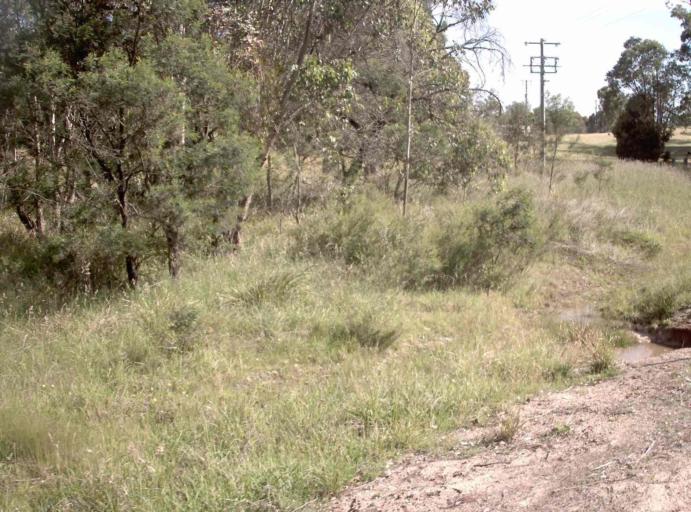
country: AU
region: Victoria
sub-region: East Gippsland
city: Lakes Entrance
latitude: -37.5281
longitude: 148.1563
